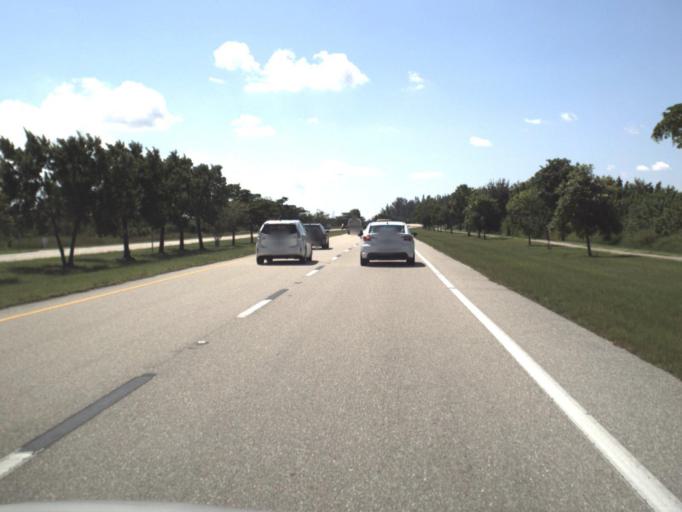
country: US
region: Florida
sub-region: Lee County
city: Pine Island Center
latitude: 26.6257
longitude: -82.0407
